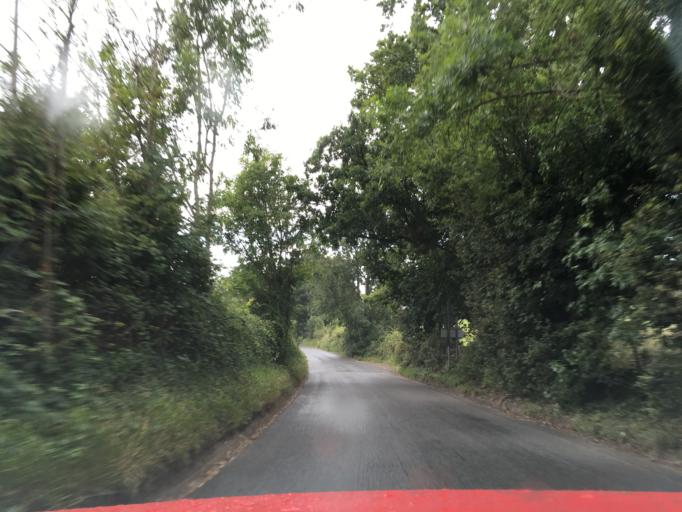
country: GB
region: England
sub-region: Kent
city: Yalding
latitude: 51.2235
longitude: 0.4755
